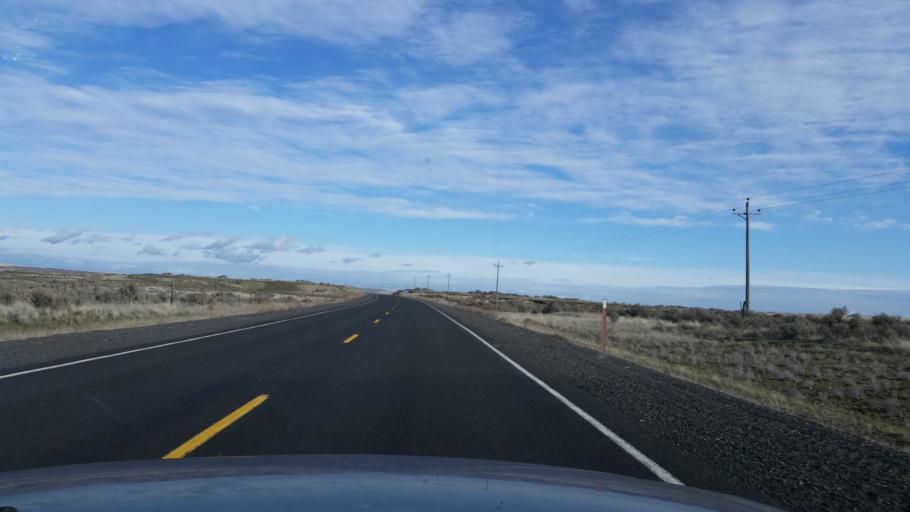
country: US
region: Washington
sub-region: Adams County
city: Ritzville
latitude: 47.3150
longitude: -118.7488
